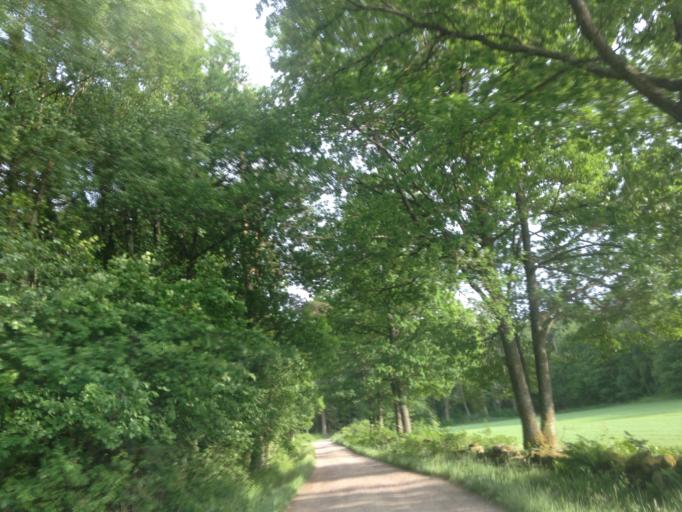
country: SE
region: Vaestra Goetaland
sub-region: Kungalvs Kommun
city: Kungalv
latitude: 57.8153
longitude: 11.9302
